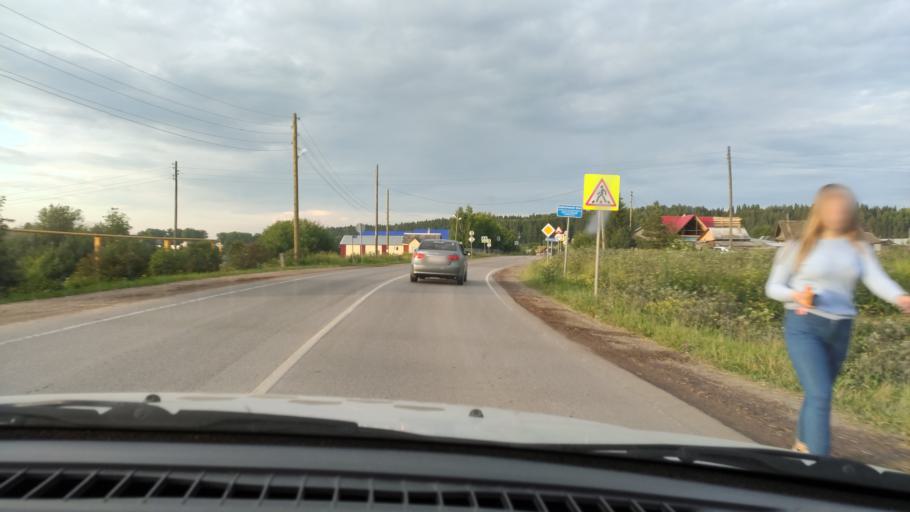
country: RU
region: Perm
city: Kukushtan
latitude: 57.4532
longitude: 56.5251
